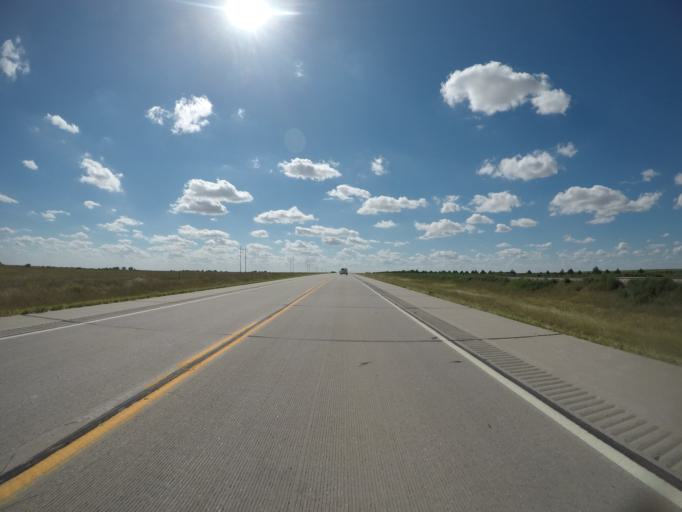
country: US
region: Colorado
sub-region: Phillips County
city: Holyoke
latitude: 40.5972
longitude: -102.3809
